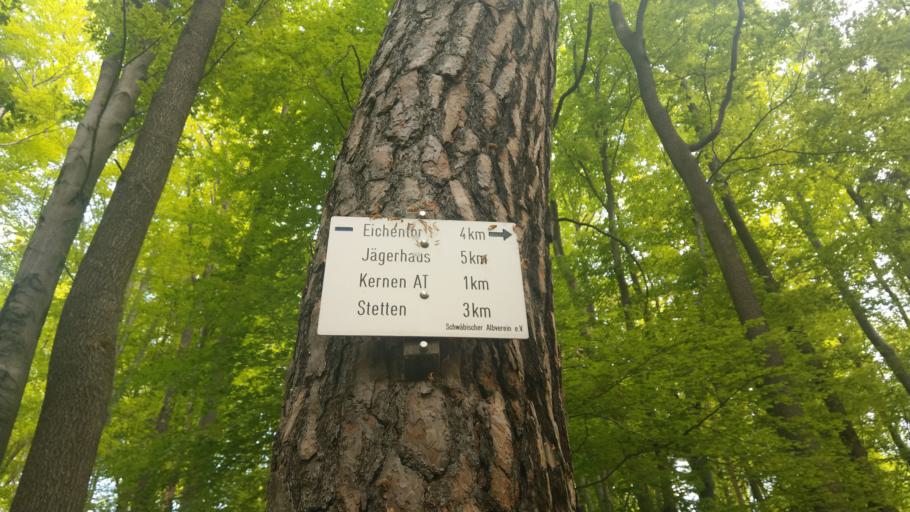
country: DE
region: Baden-Wuerttemberg
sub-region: Regierungsbezirk Stuttgart
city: Esslingen
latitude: 48.7779
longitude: 9.3100
